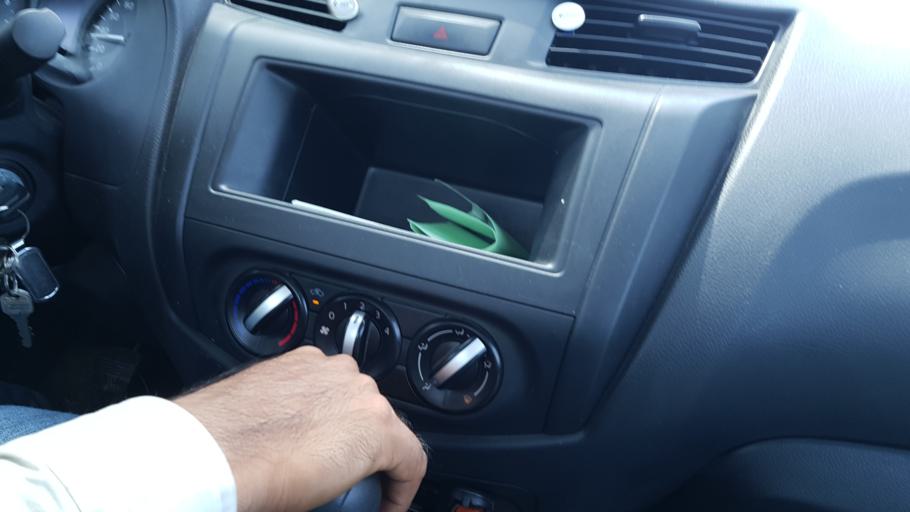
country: MX
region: Tabasco
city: Aquiles Serdan
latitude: 17.7539
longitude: -92.1524
